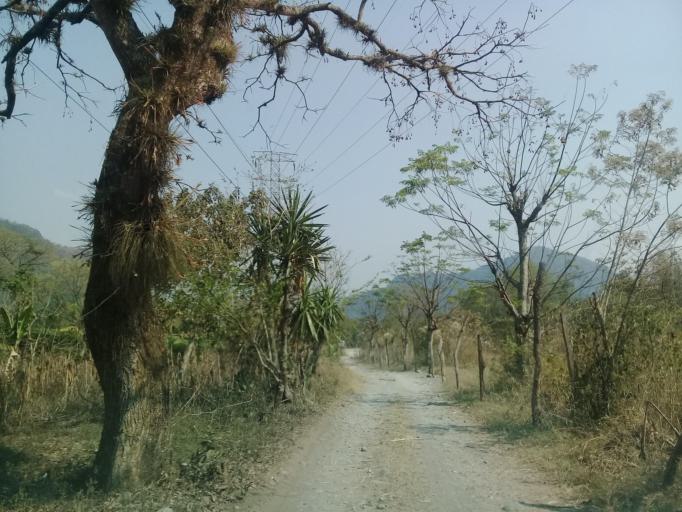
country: MX
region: Veracruz
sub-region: Ixtaczoquitlan
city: Campo Chico
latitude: 18.8316
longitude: -97.0228
